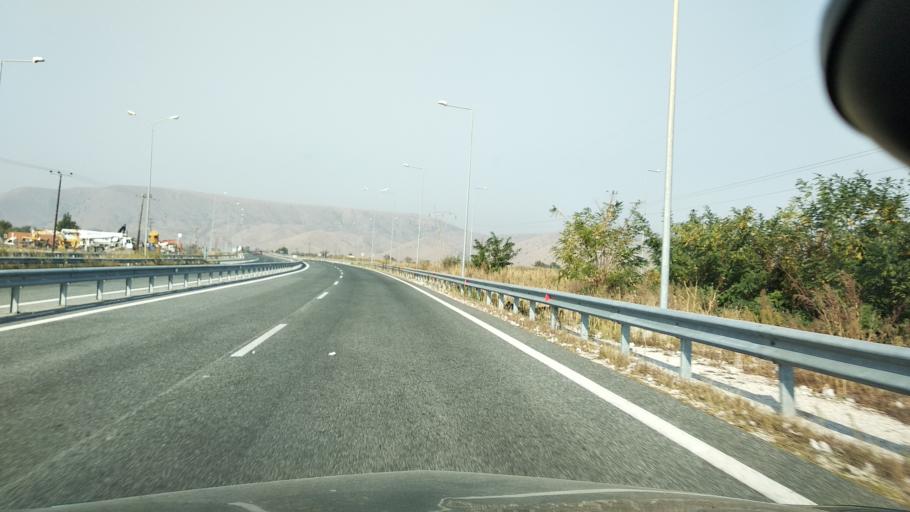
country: GR
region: Thessaly
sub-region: Trikala
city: Zarkos
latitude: 39.5940
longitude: 22.1229
